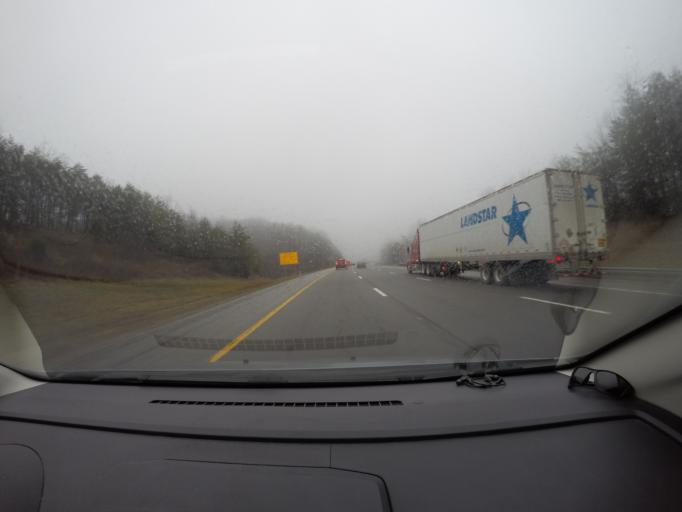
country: US
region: Tennessee
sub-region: Marion County
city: Monteagle
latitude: 35.2136
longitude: -85.8192
